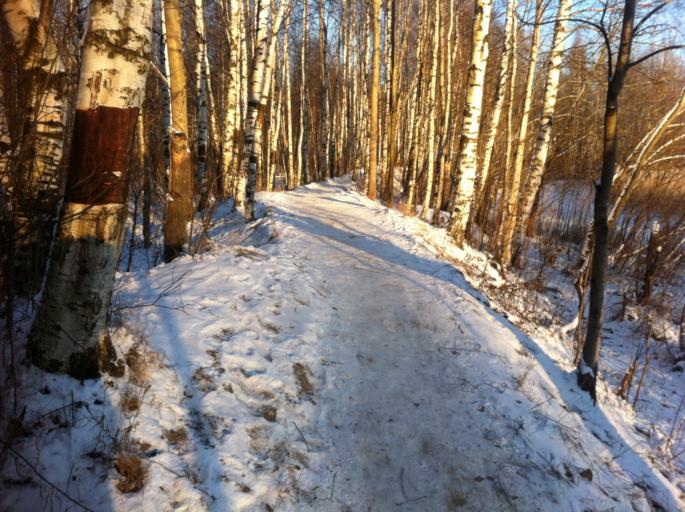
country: RU
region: St.-Petersburg
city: Uritsk
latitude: 59.8554
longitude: 30.1637
